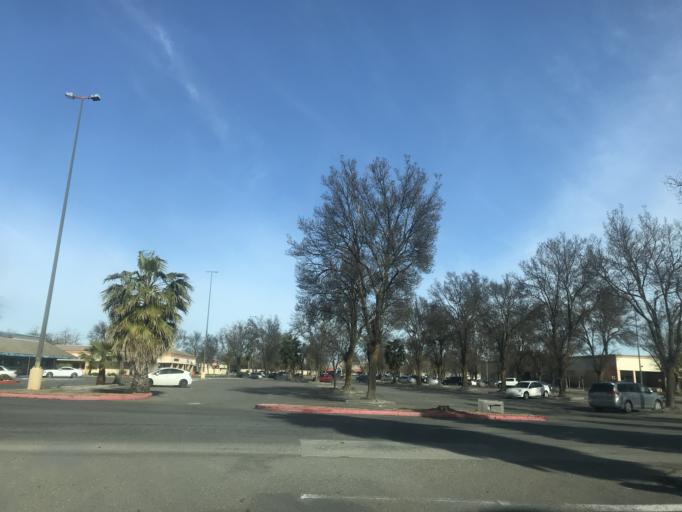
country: US
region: California
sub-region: Yolo County
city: Woodland
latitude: 38.6598
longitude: -121.7649
